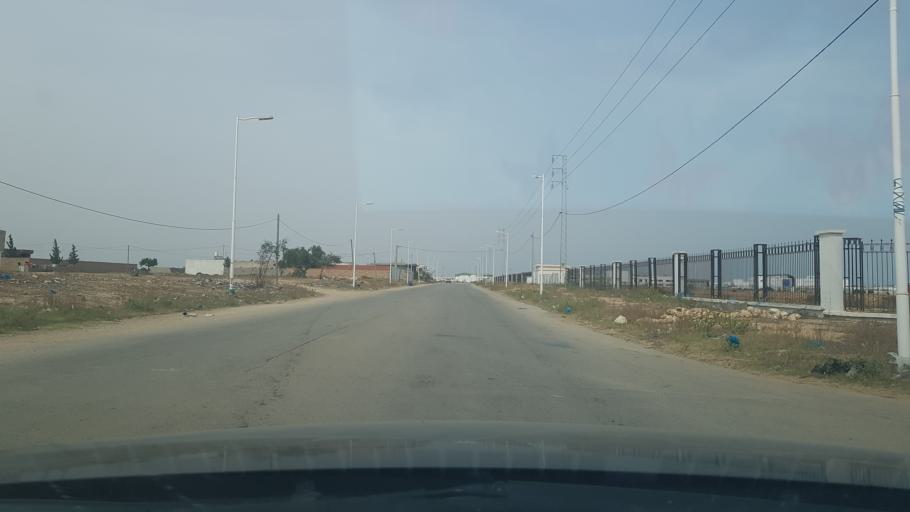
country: TN
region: Safaqis
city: Al Qarmadah
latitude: 34.8364
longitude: 10.7479
